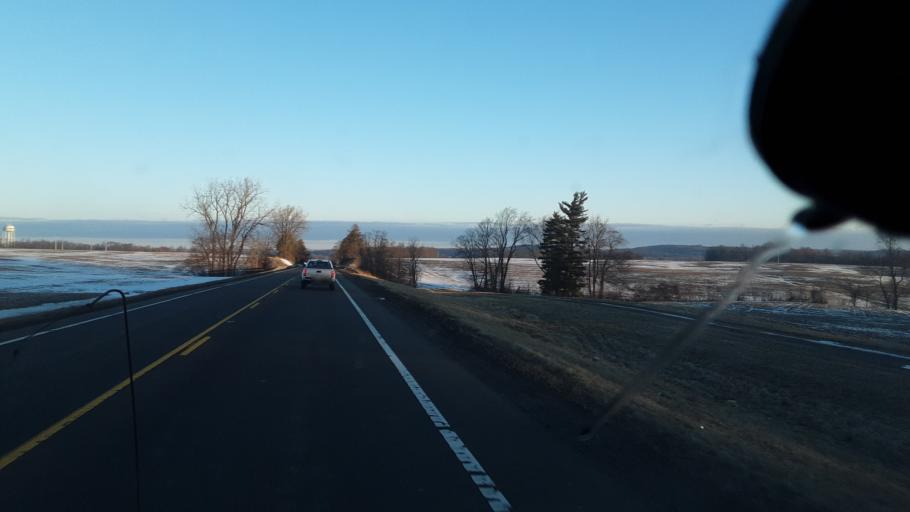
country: US
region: Ohio
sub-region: Perry County
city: Thornport
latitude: 39.8862
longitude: -82.4042
